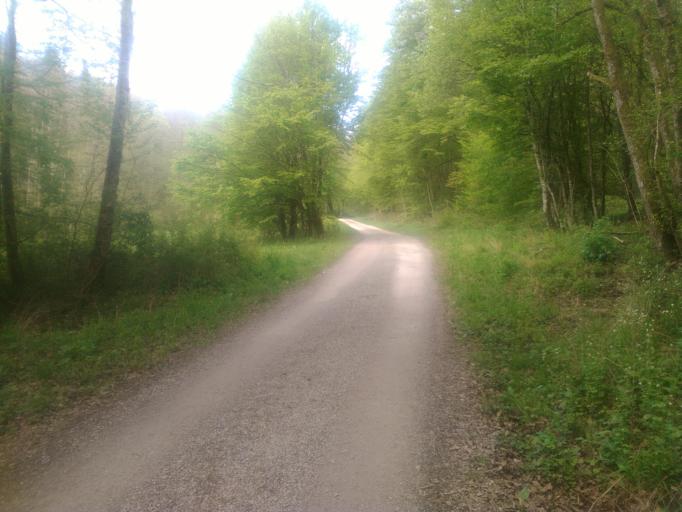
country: DE
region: Baden-Wuerttemberg
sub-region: Regierungsbezirk Stuttgart
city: Schlaitdorf
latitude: 48.6055
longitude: 9.1726
